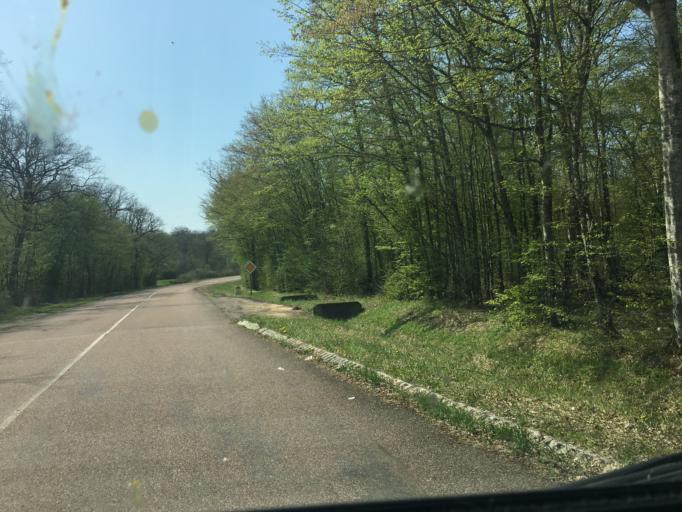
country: FR
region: Lorraine
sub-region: Departement de la Meuse
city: Vigneulles-les-Hattonchatel
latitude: 48.9483
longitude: 5.7388
